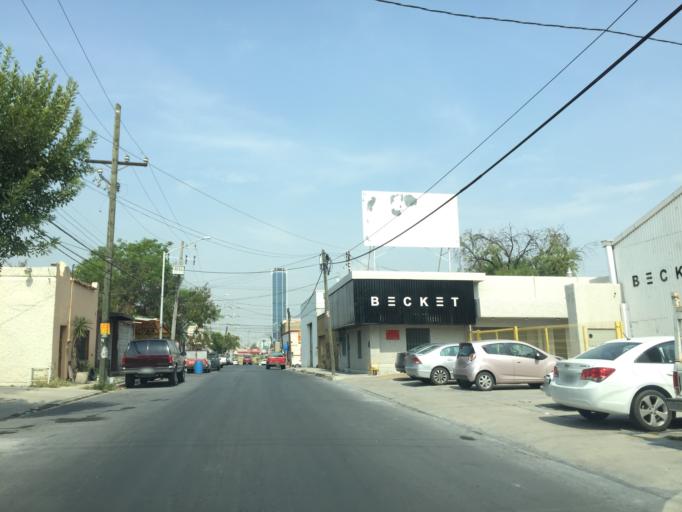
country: MX
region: Nuevo Leon
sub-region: Monterrey
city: Monterrey
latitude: 25.6620
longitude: -100.3030
